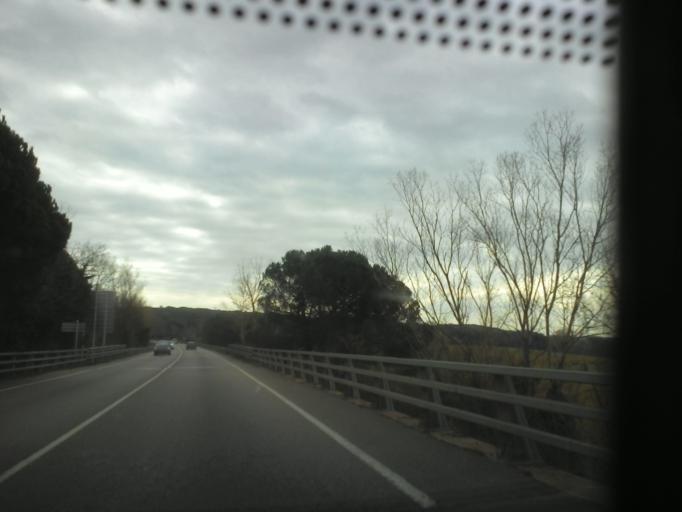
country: ES
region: Catalonia
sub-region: Provincia de Girona
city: Fornells de la Selva
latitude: 41.9393
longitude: 2.8207
